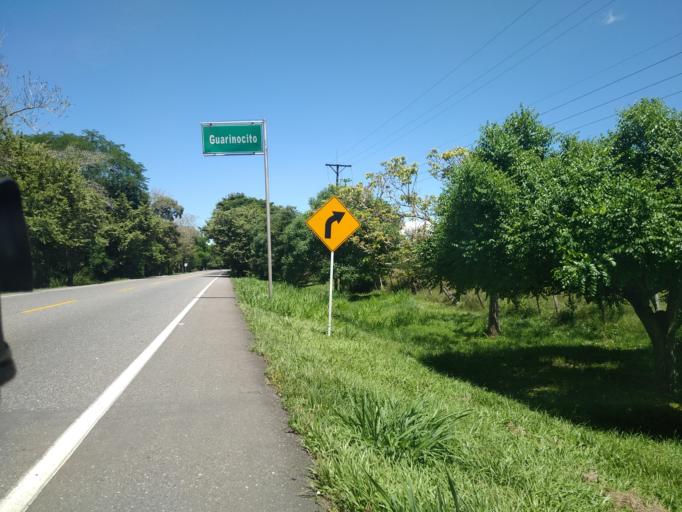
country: CO
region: Caldas
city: La Dorada
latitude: 5.3474
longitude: -74.7331
